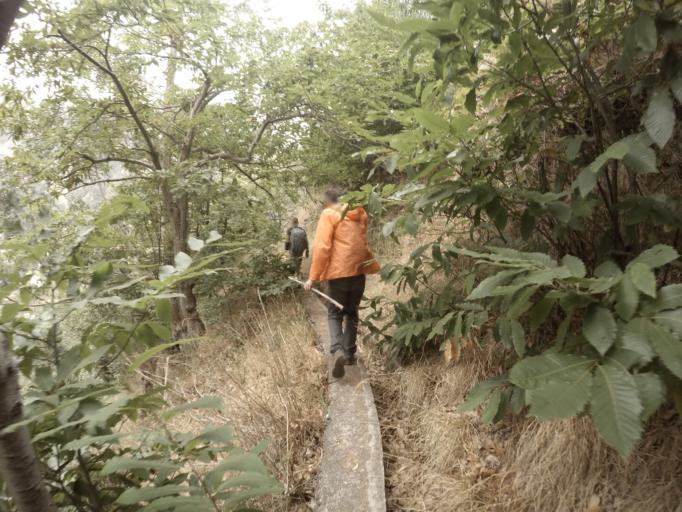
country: PT
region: Madeira
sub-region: Camara de Lobos
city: Curral das Freiras
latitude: 32.7086
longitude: -16.9687
